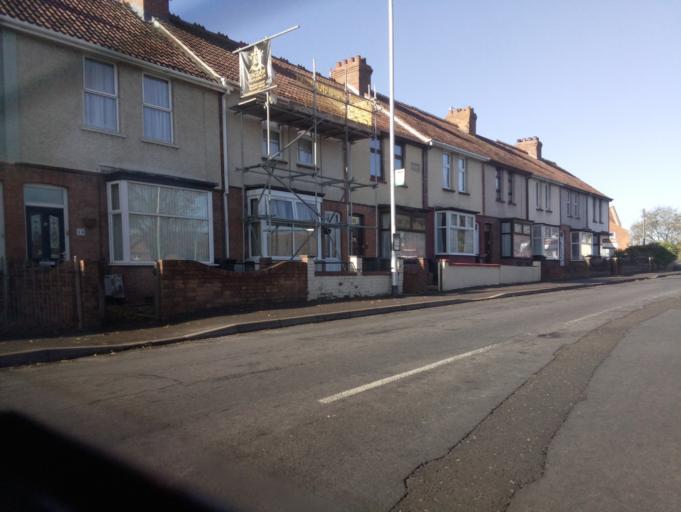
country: GB
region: England
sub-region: Somerset
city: Bridgwater
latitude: 51.1259
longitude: -2.9878
